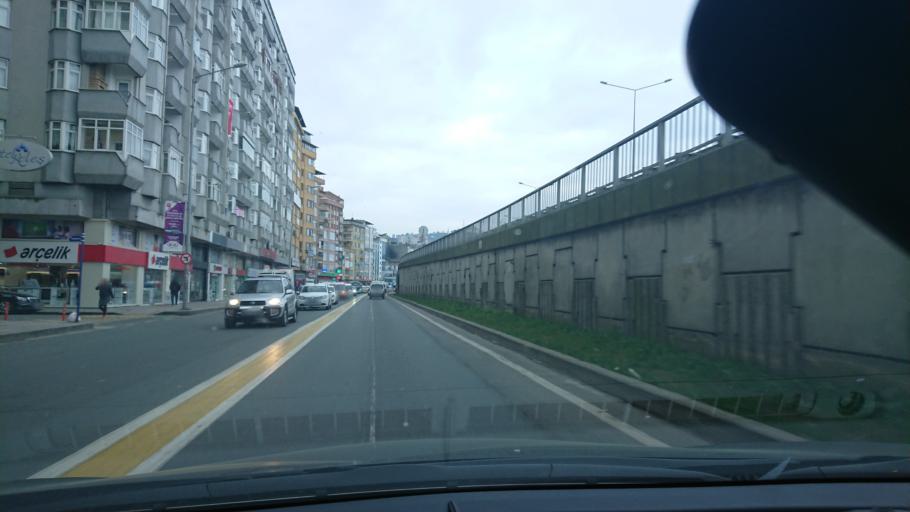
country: TR
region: Rize
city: Rize
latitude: 41.0257
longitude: 40.5239
